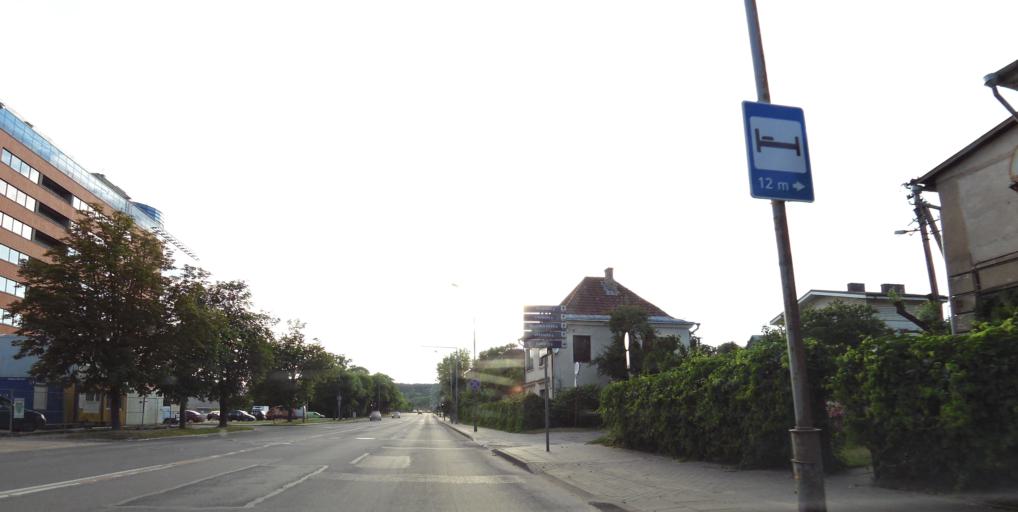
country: LT
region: Vilnius County
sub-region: Vilnius
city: Vilnius
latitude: 54.7042
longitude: 25.2781
